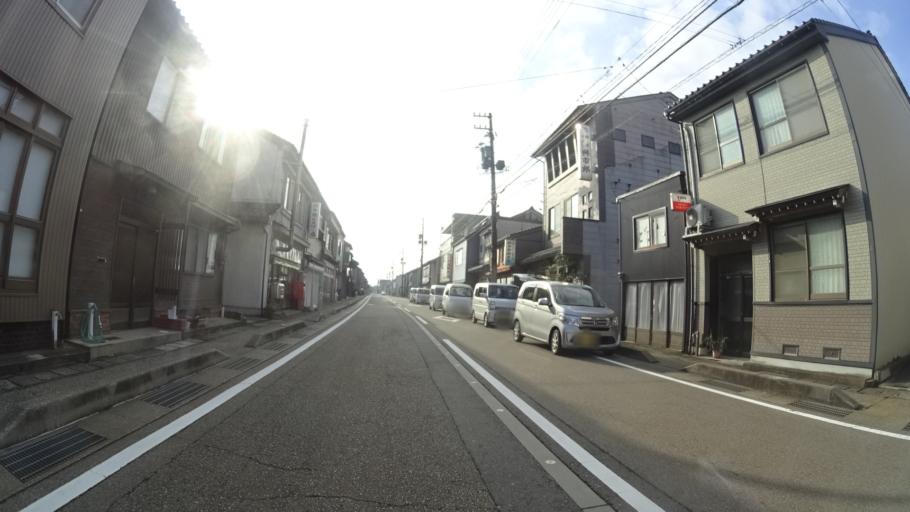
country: JP
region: Toyama
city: Himi
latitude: 36.8679
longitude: 136.9834
